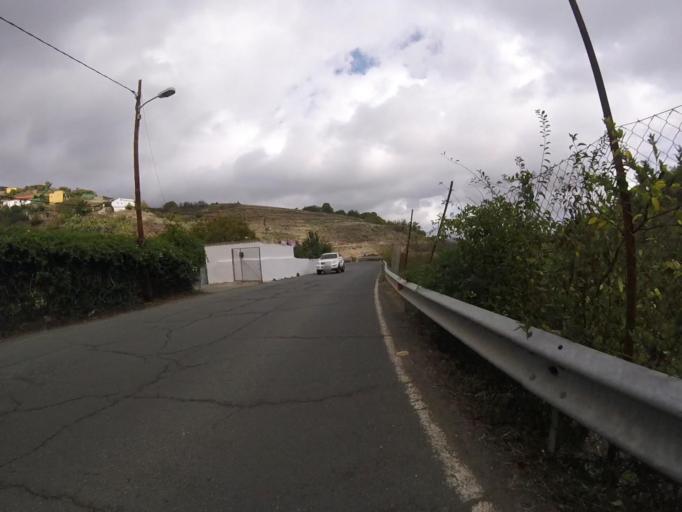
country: ES
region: Canary Islands
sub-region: Provincia de Las Palmas
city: Vega de San Mateo
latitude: 27.9937
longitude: -15.5676
